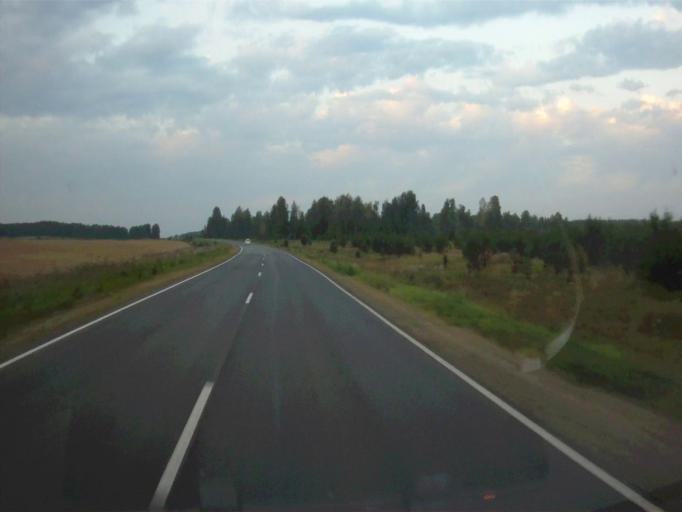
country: RU
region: Chelyabinsk
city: Chebarkul'
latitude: 55.1600
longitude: 60.4408
